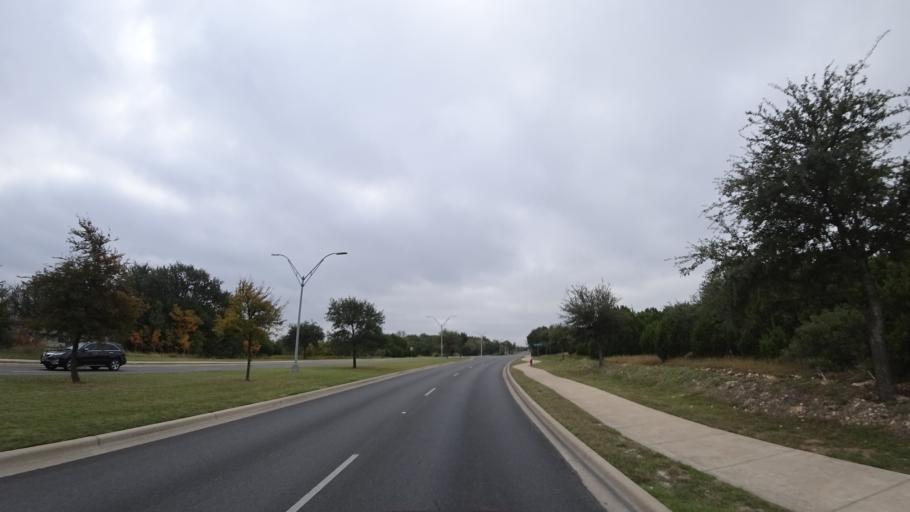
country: US
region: Texas
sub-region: Williamson County
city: Cedar Park
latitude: 30.5094
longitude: -97.8490
